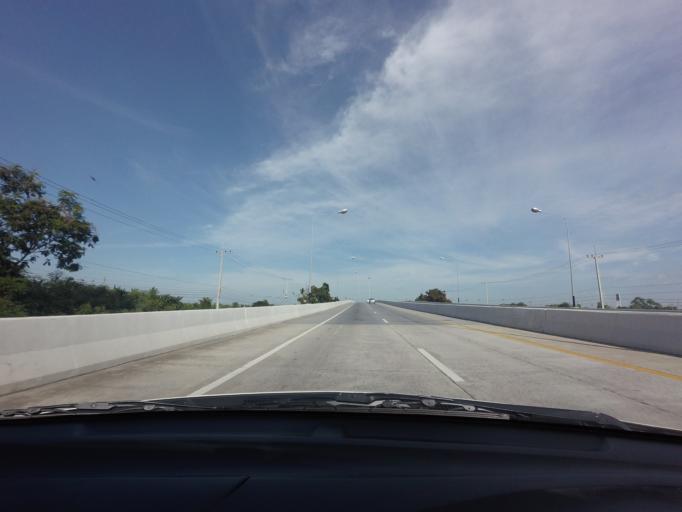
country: TH
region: Suphan Buri
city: Suphan Buri
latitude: 14.4657
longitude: 100.0454
